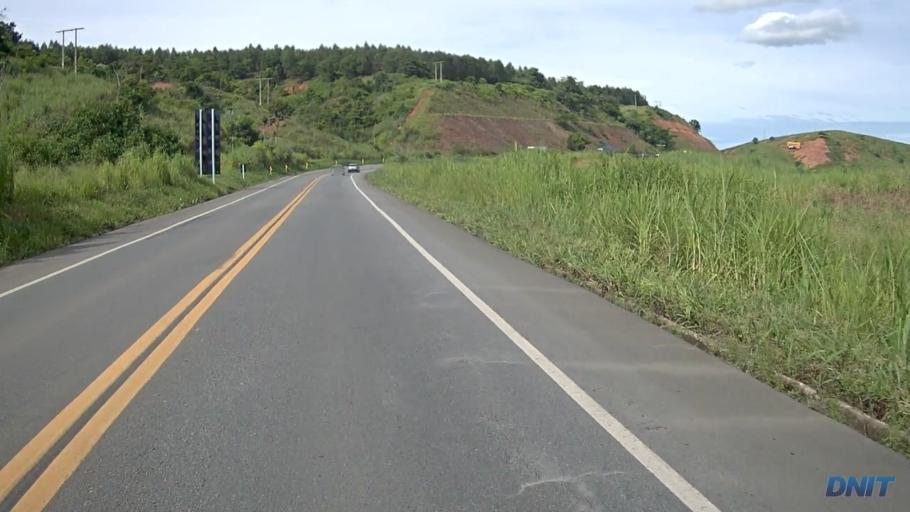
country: BR
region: Minas Gerais
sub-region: Belo Oriente
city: Belo Oriente
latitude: -19.2667
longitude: -42.3532
